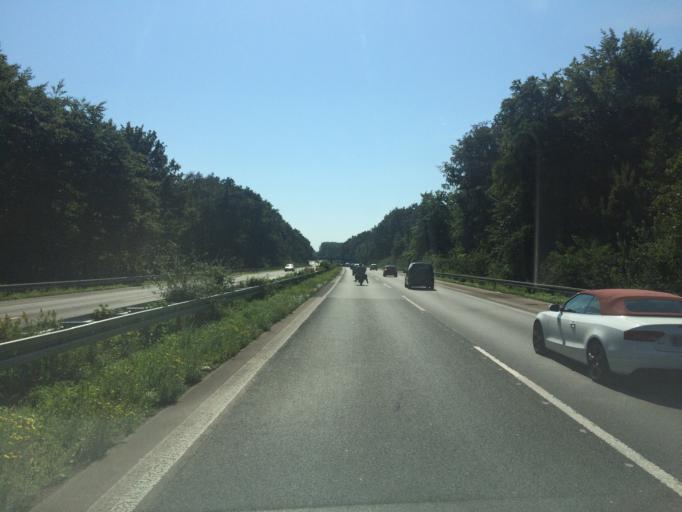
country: DE
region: North Rhine-Westphalia
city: Bergkamen
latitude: 51.6305
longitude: 7.6862
